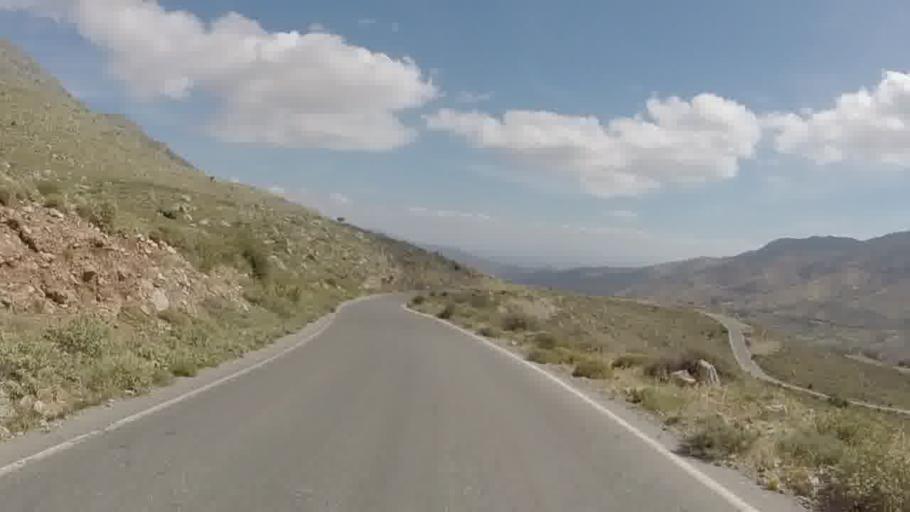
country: GR
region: Crete
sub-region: Nomos Rethymnis
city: Agia Galini
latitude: 35.1550
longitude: 24.6200
